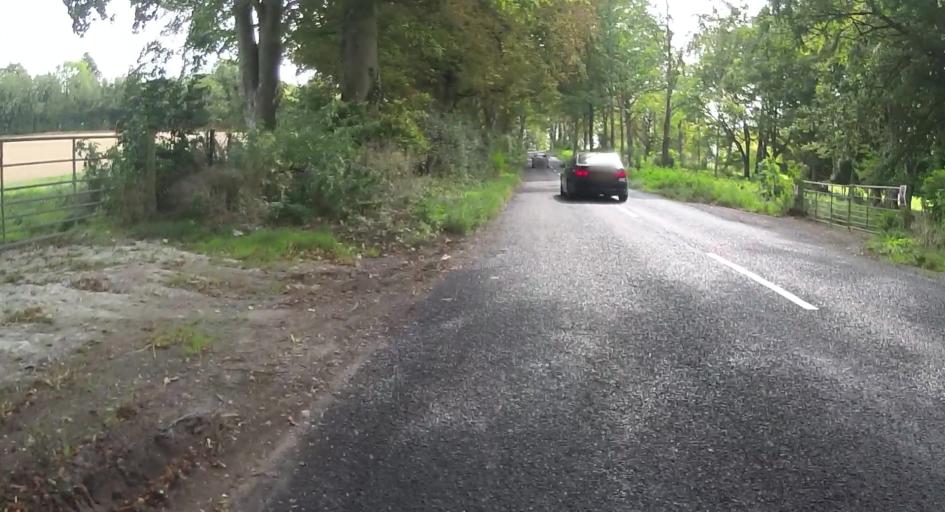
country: GB
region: England
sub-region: Hampshire
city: Kings Worthy
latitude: 51.0743
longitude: -1.1733
